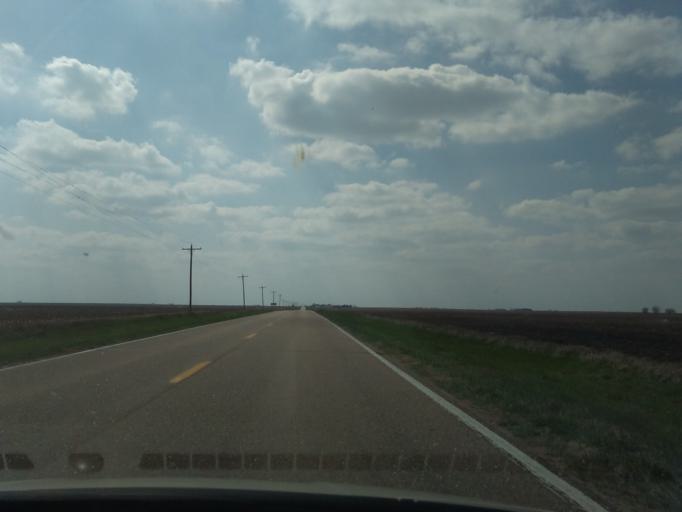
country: US
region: Nebraska
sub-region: Nuckolls County
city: Nelson
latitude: 40.1473
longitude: -98.0104
